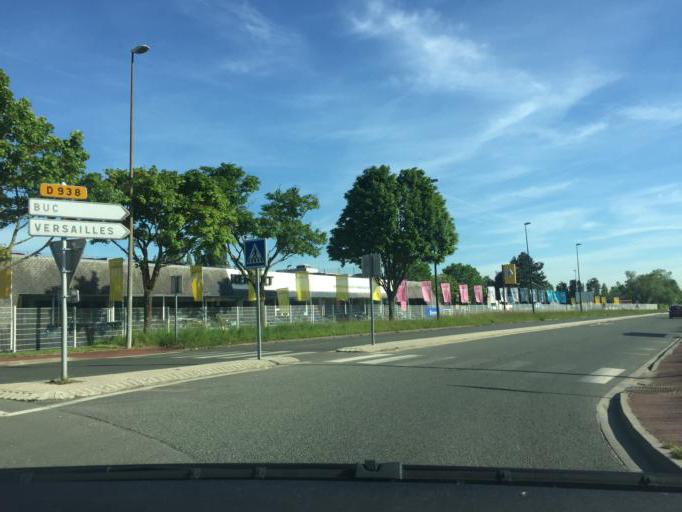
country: FR
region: Ile-de-France
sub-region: Departement des Yvelines
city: Les Loges-en-Josas
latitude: 48.7609
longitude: 2.1249
